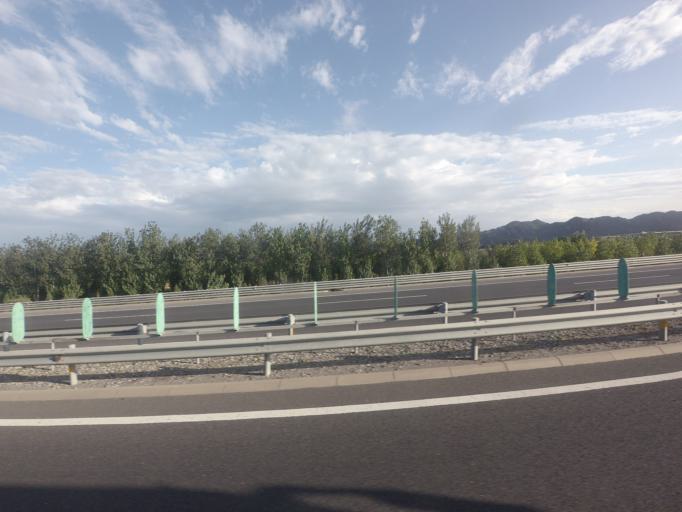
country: CN
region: Beijing
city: Gulou
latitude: 40.3557
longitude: 116.8511
